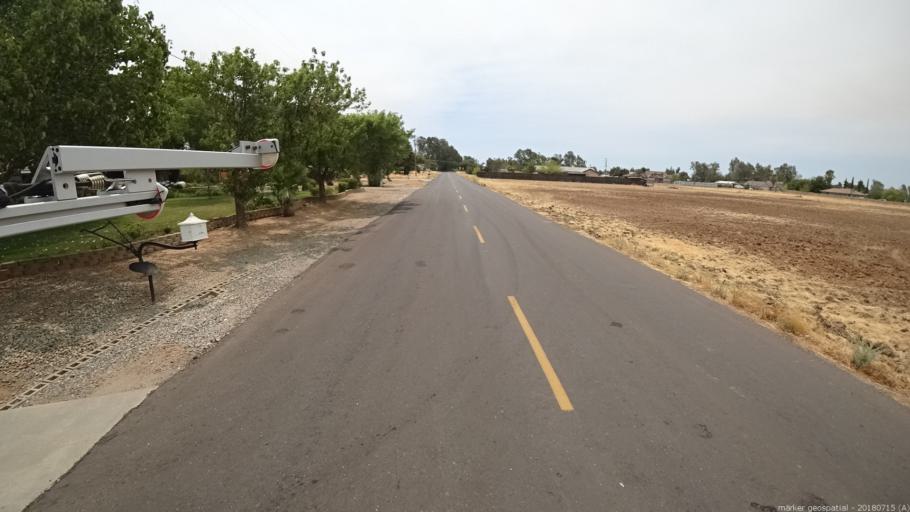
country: US
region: California
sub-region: Madera County
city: Madera Acres
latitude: 37.0087
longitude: -120.0891
